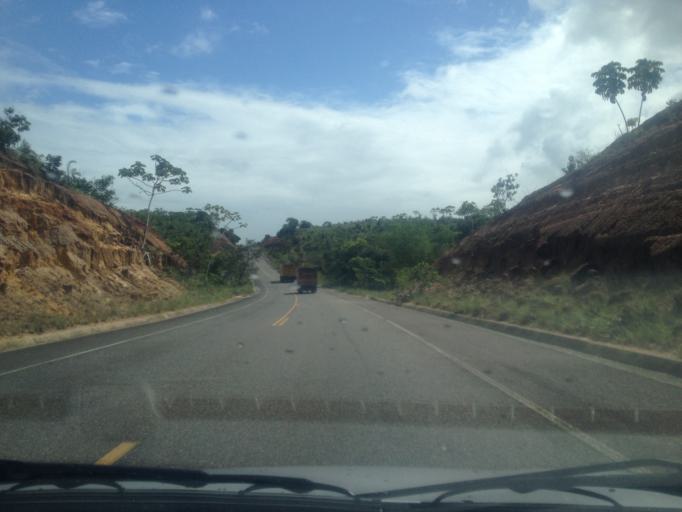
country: BR
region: Sergipe
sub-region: Indiaroba
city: Indiaroba
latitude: -11.5690
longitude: -37.5541
